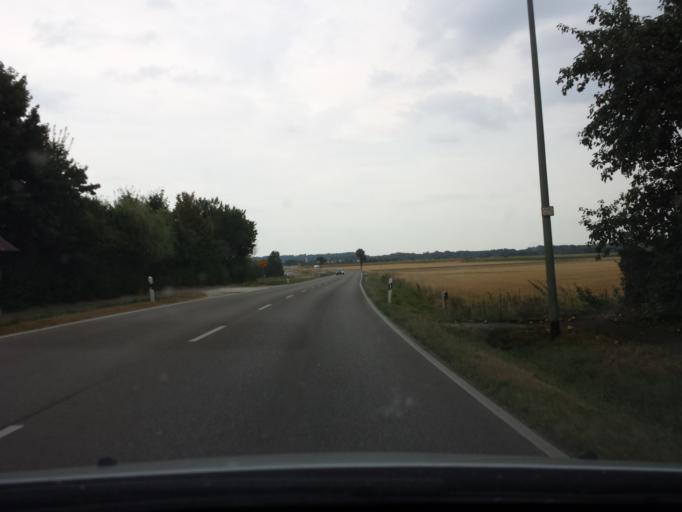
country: DE
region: Bavaria
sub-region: Swabia
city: Neu-Ulm
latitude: 48.4075
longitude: 10.0487
